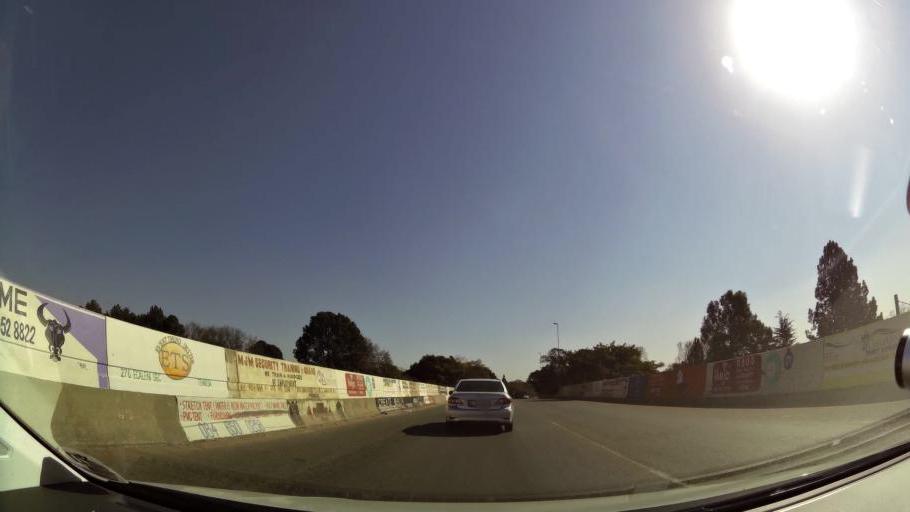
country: ZA
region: Gauteng
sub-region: Ekurhuleni Metropolitan Municipality
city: Tembisa
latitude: -26.0329
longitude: 28.2549
